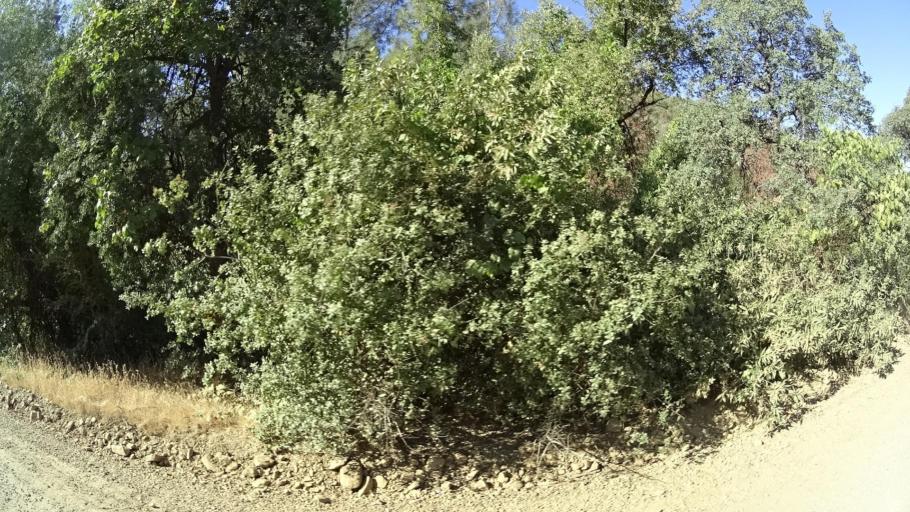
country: US
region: California
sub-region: Mariposa County
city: Mariposa
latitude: 37.6169
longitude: -120.2091
